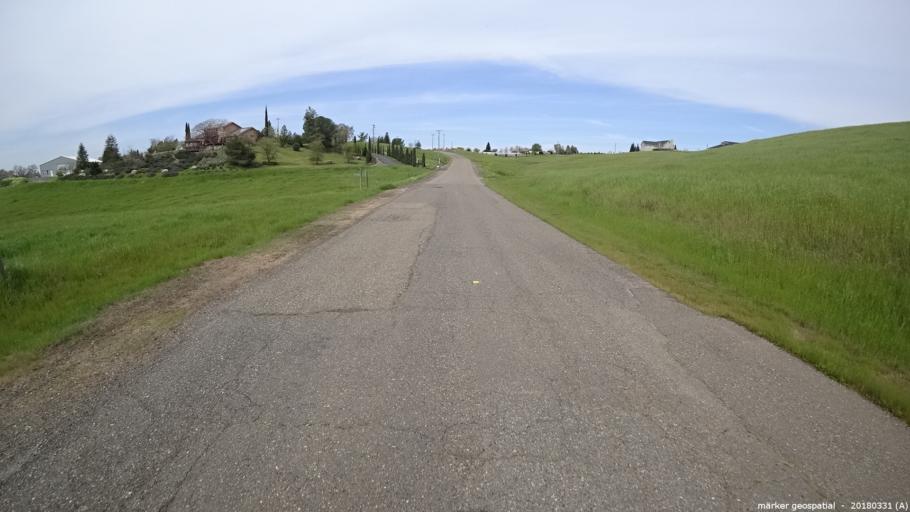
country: US
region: California
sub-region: Sacramento County
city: Rancho Murieta
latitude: 38.4904
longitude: -121.1420
